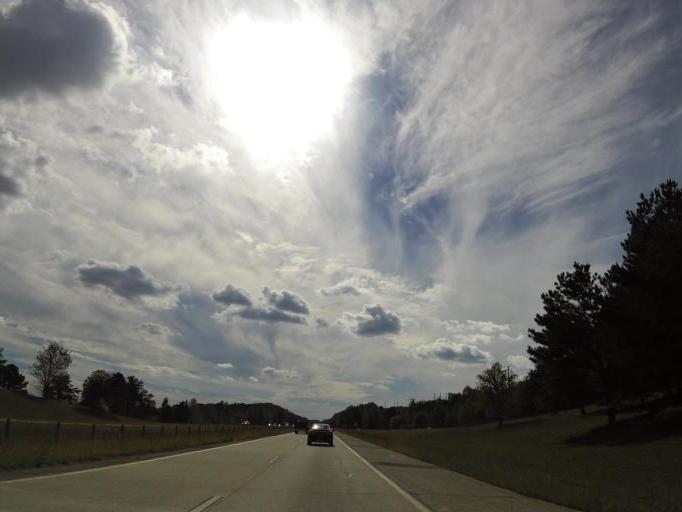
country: US
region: Georgia
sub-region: Cherokee County
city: Ball Ground
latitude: 34.3001
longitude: -84.4250
